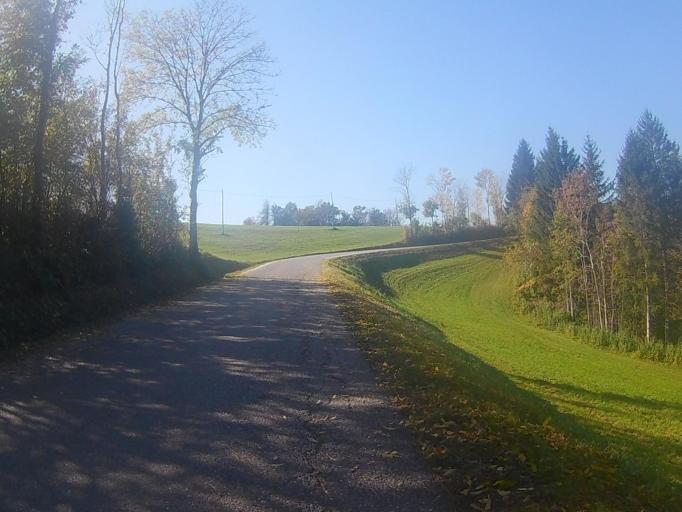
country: SI
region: Race-Fram
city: Morje
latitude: 46.4680
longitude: 15.5899
